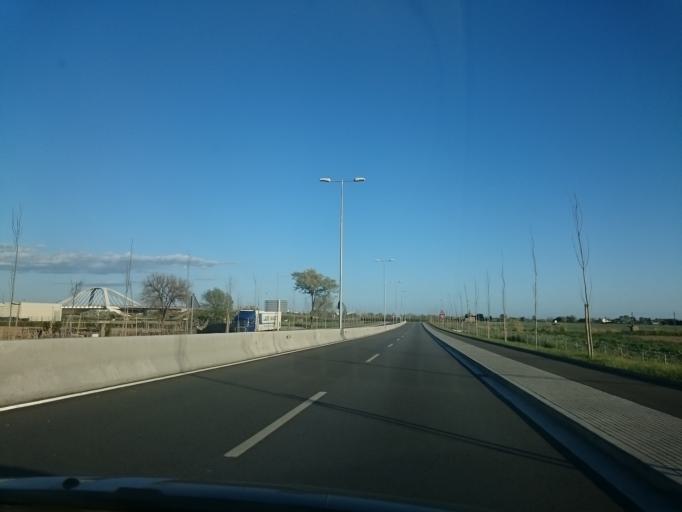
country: ES
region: Catalonia
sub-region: Provincia de Barcelona
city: El Prat de Llobregat
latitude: 41.3231
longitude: 2.1082
